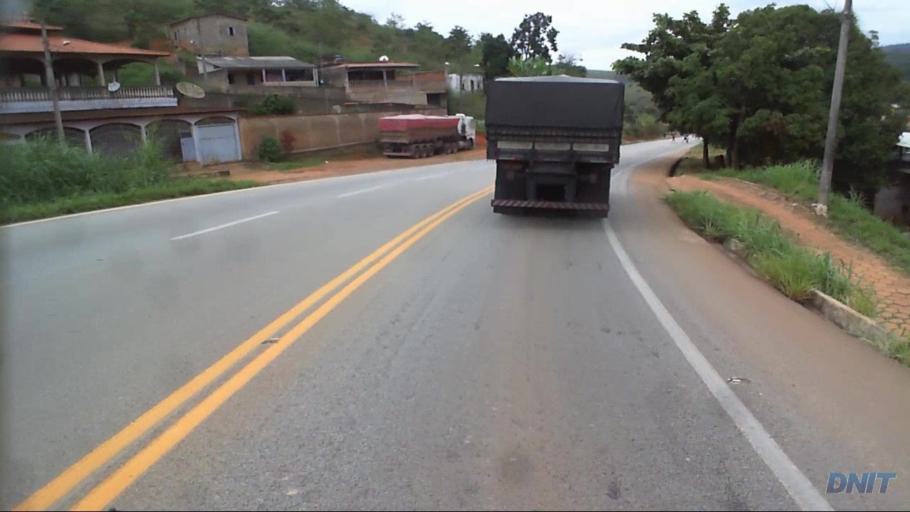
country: BR
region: Minas Gerais
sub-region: Nova Era
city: Nova Era
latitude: -19.8164
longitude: -43.0665
